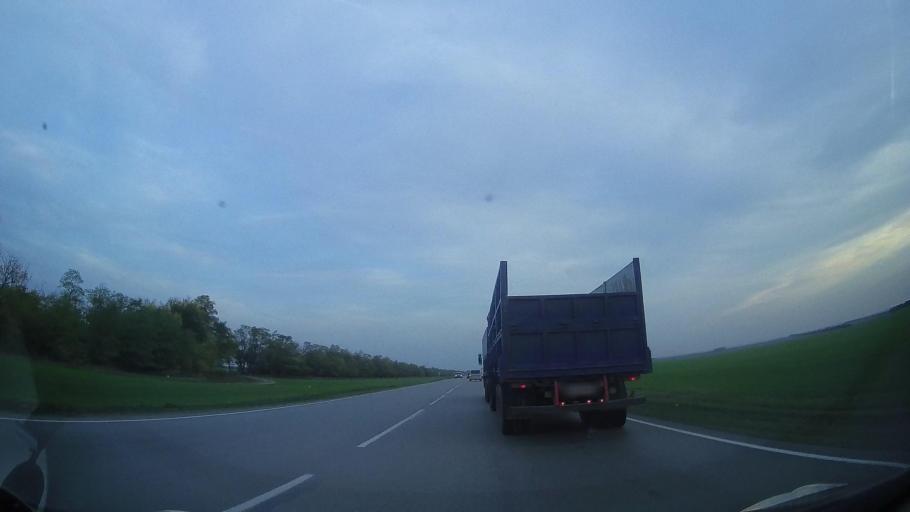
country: RU
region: Rostov
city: Kagal'nitskaya
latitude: 46.9161
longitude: 40.1088
